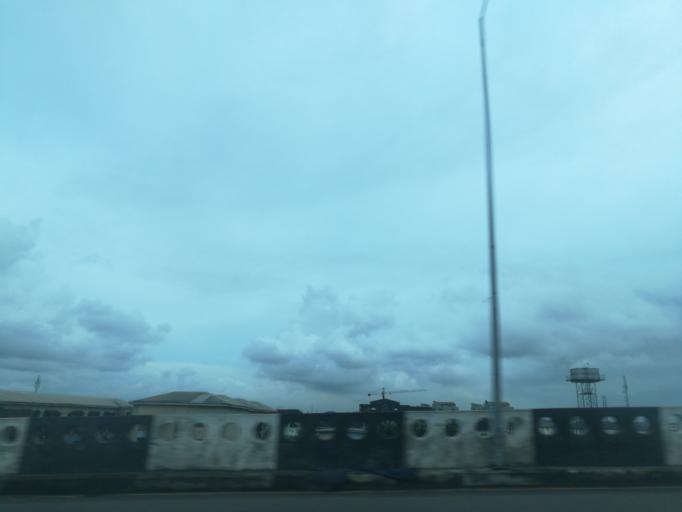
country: NG
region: Rivers
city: Port Harcourt
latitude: 4.8150
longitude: 6.9835
